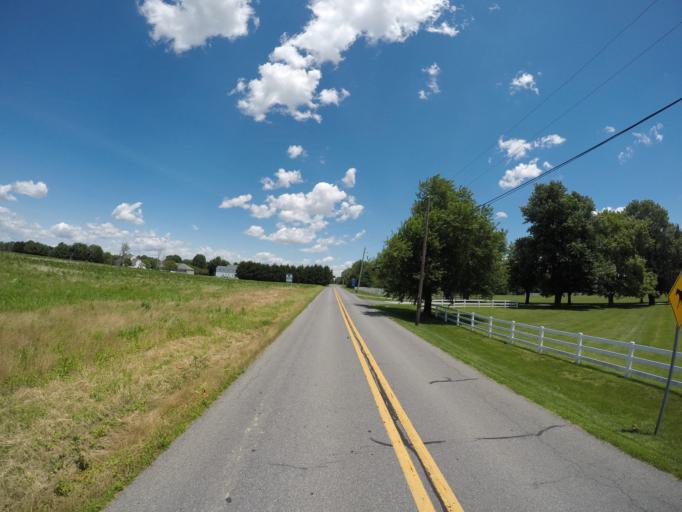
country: US
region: Delaware
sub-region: New Castle County
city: Middletown
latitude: 39.4809
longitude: -75.7724
